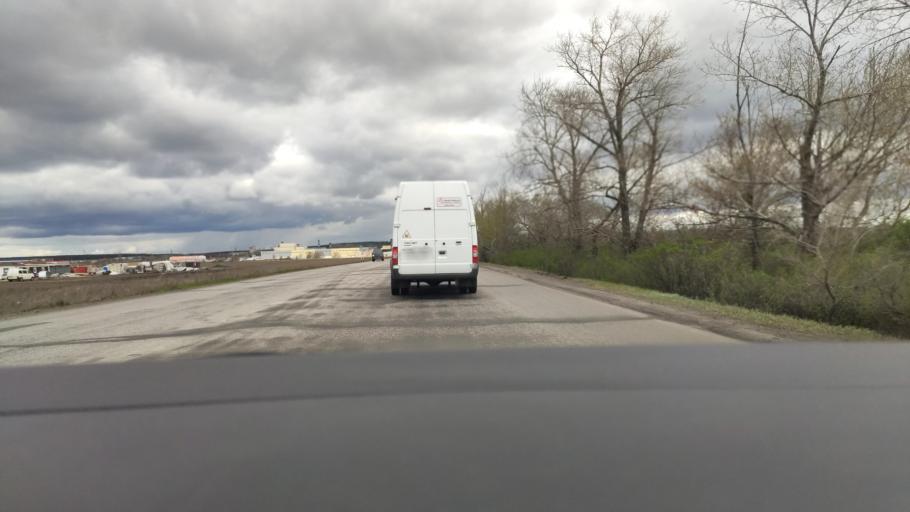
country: RU
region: Voronezj
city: Maslovka
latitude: 51.5420
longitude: 39.2865
